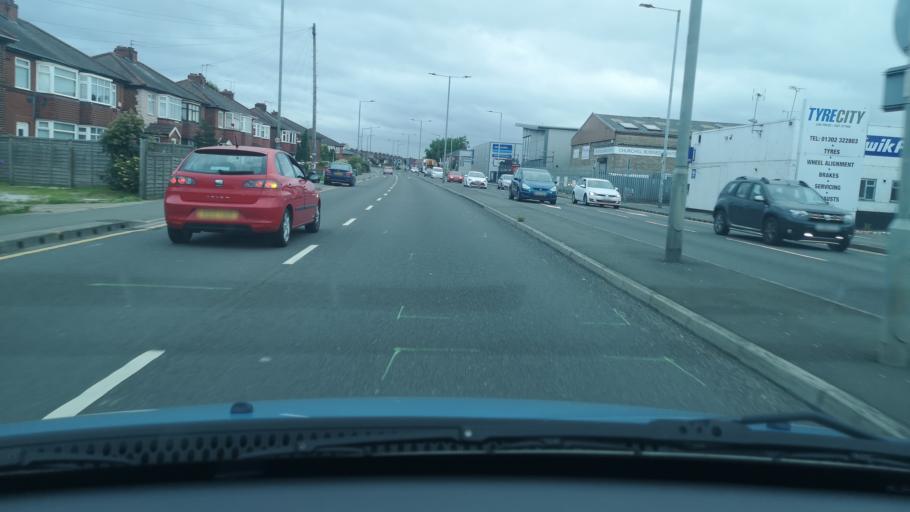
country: GB
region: England
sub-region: Doncaster
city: Doncaster
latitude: 53.5355
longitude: -1.1218
